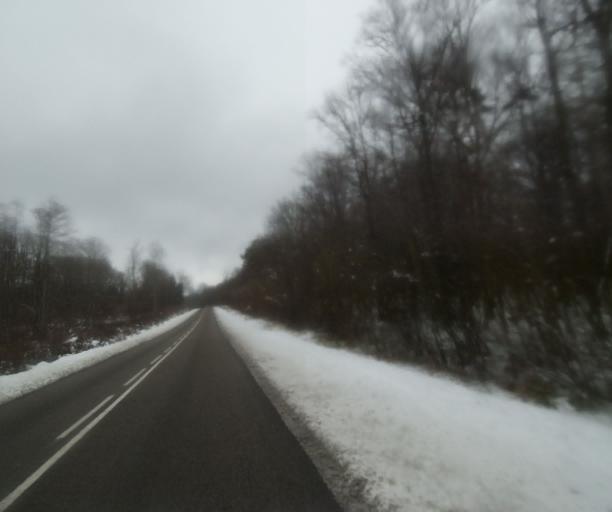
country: FR
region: Champagne-Ardenne
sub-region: Departement de la Haute-Marne
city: Montier-en-Der
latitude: 48.4848
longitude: 4.8227
